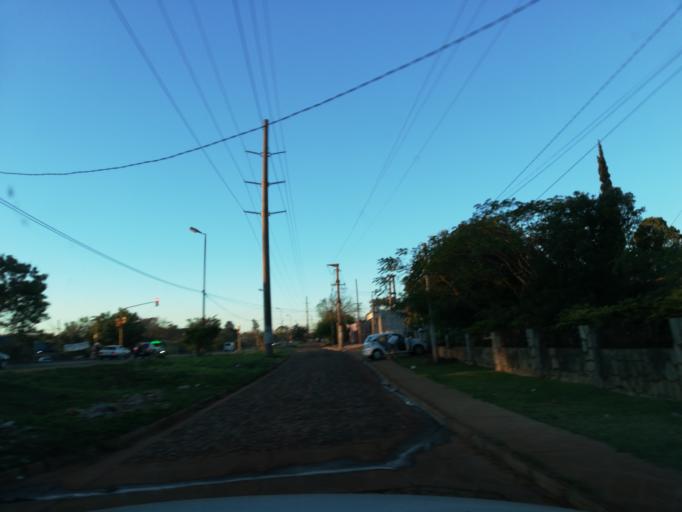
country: AR
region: Misiones
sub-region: Departamento de Capital
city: Posadas
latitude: -27.4195
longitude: -55.9307
